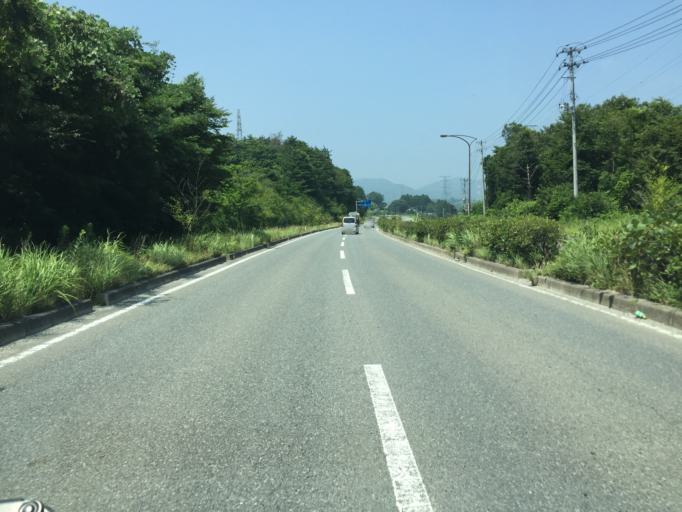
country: JP
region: Miyagi
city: Marumori
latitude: 37.8380
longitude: 140.9150
